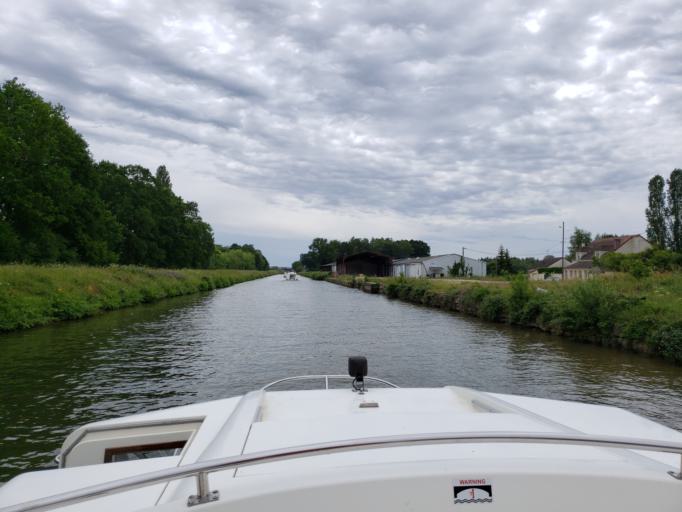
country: FR
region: Bourgogne
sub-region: Departement de l'Yonne
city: Appoigny
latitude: 47.8863
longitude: 3.5441
